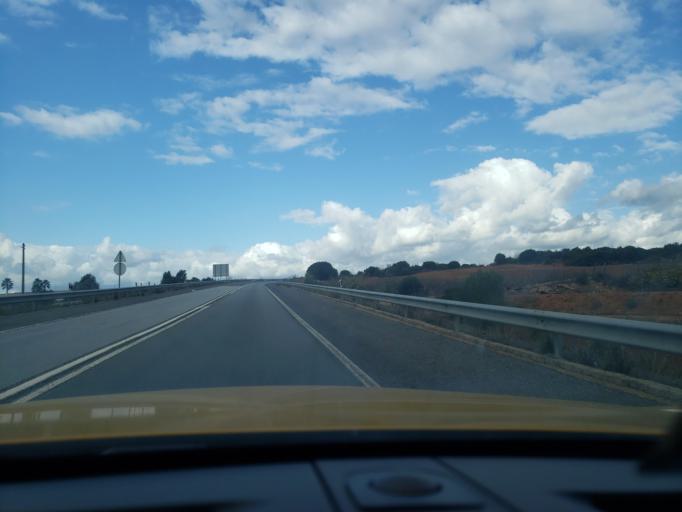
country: PT
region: Faro
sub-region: Portimao
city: Alvor
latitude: 37.1641
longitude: -8.5698
